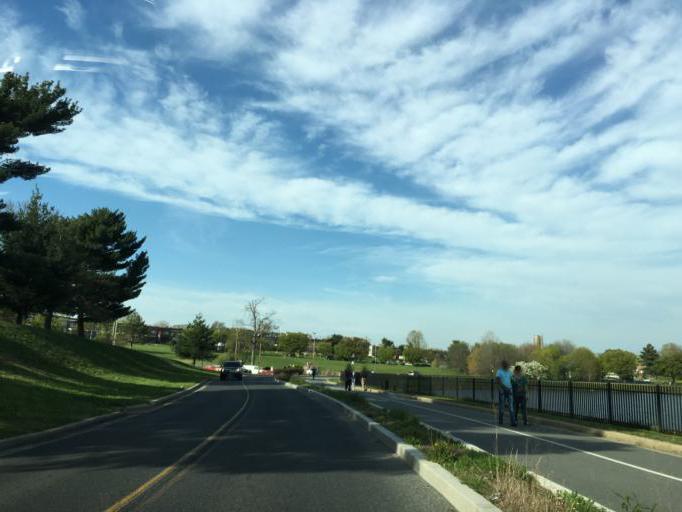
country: US
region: Maryland
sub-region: City of Baltimore
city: Baltimore
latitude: 39.3295
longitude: -76.5852
